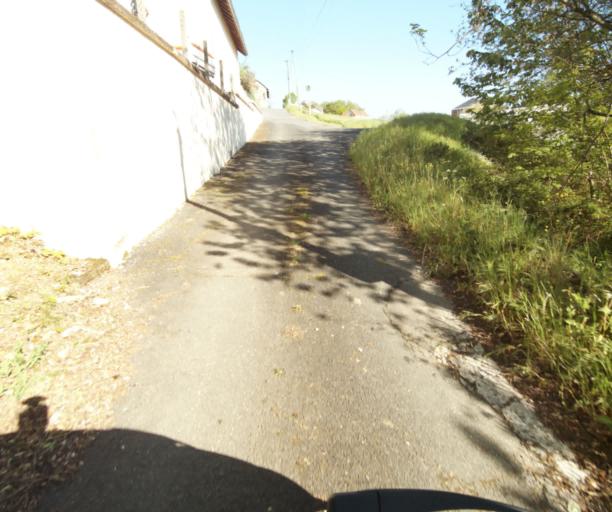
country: FR
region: Limousin
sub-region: Departement de la Correze
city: Tulle
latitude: 45.2597
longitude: 1.7749
